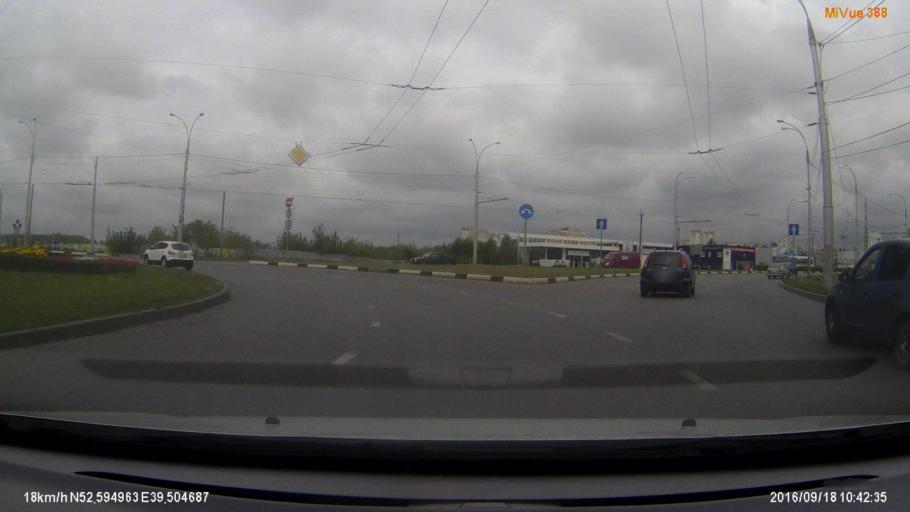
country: RU
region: Lipetsk
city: Syrskoye
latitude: 52.5949
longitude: 39.5047
